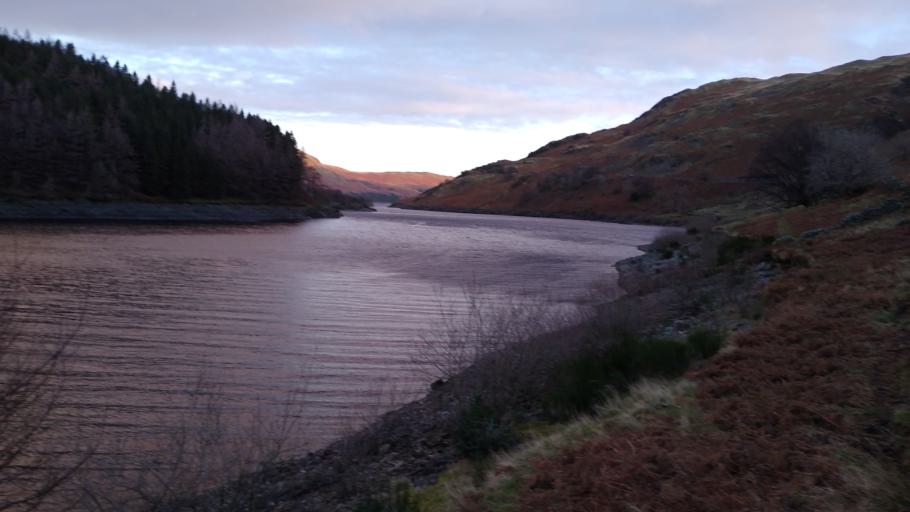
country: GB
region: England
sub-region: Cumbria
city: Windermere
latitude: 54.4941
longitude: -2.8105
